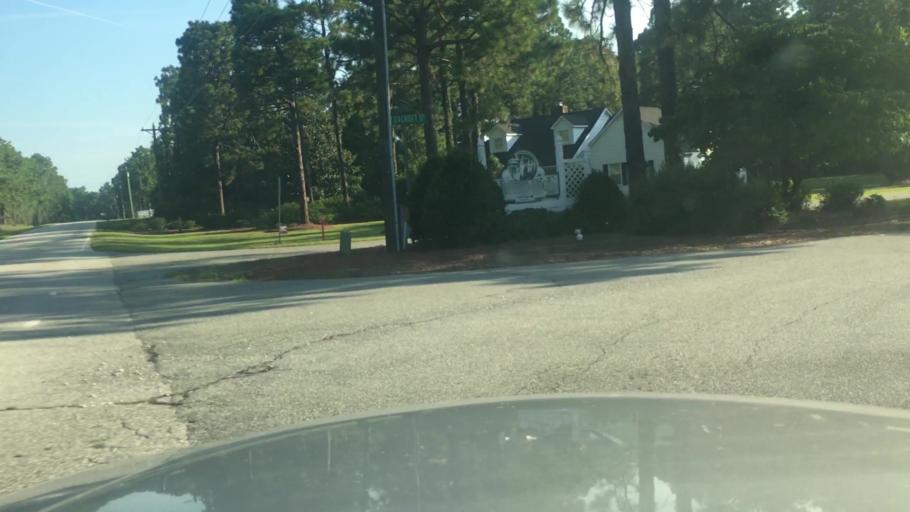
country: US
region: North Carolina
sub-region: Harnett County
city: Walkertown
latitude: 35.2188
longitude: -78.8655
